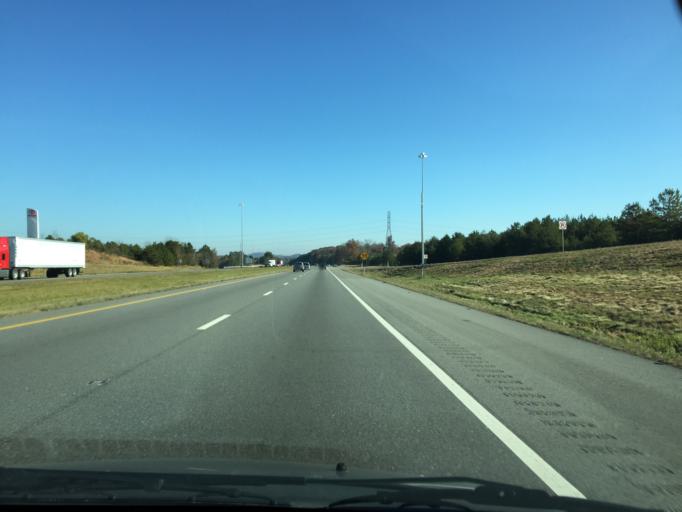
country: US
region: Tennessee
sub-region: Bradley County
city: Cleveland
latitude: 35.1530
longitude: -84.9461
